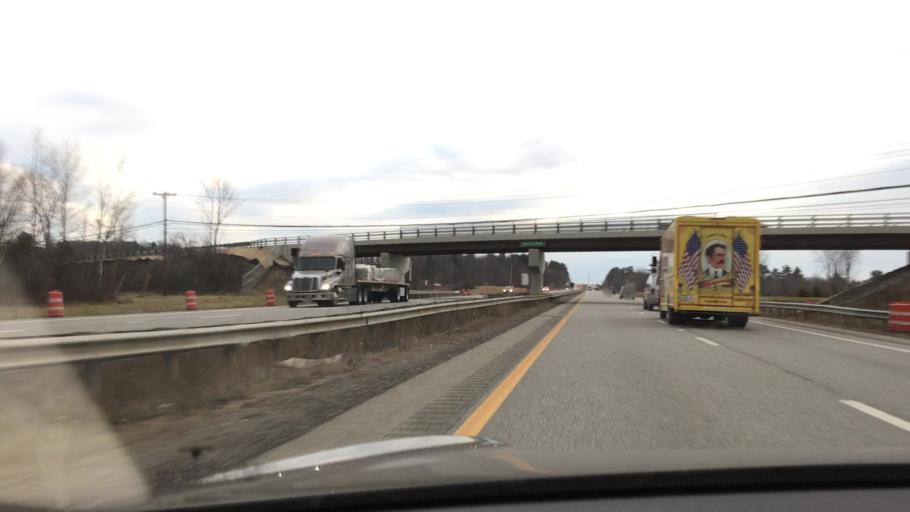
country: US
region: Maine
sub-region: Kennebec County
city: Hallowell
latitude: 44.2980
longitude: -69.8075
